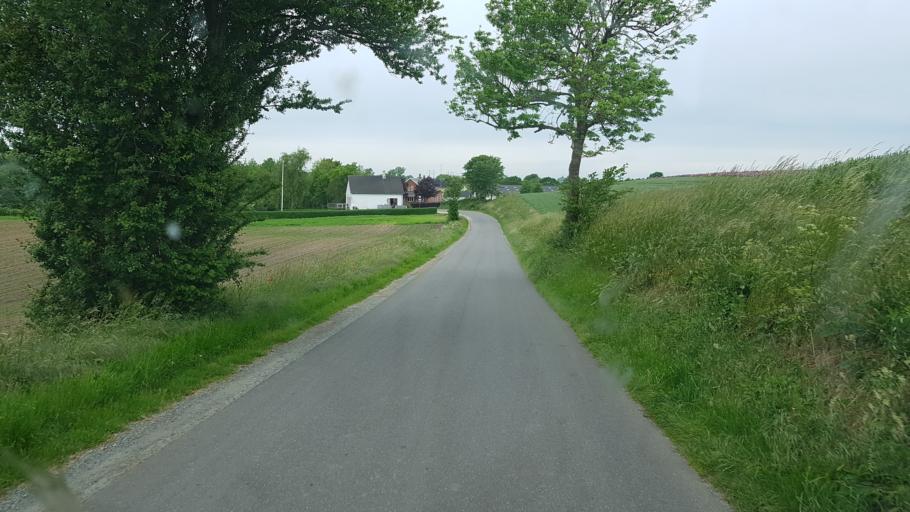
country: DK
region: South Denmark
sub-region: Nordfyns Kommune
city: Bogense
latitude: 55.4735
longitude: 10.0699
